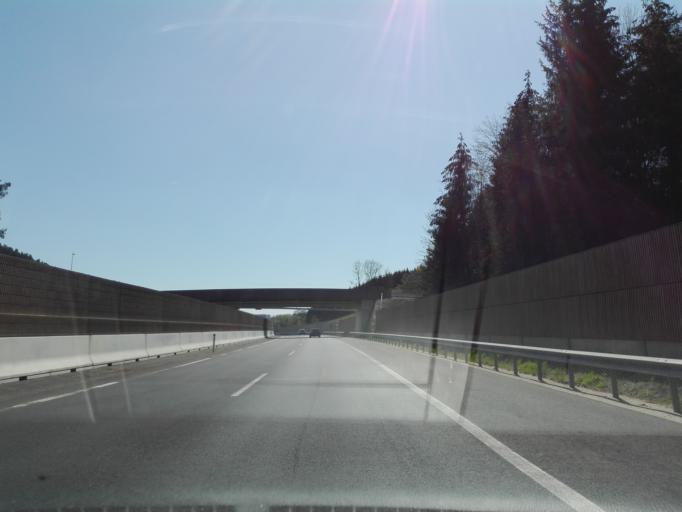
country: AT
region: Upper Austria
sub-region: Politischer Bezirk Freistadt
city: Freistadt
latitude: 48.4424
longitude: 14.4836
